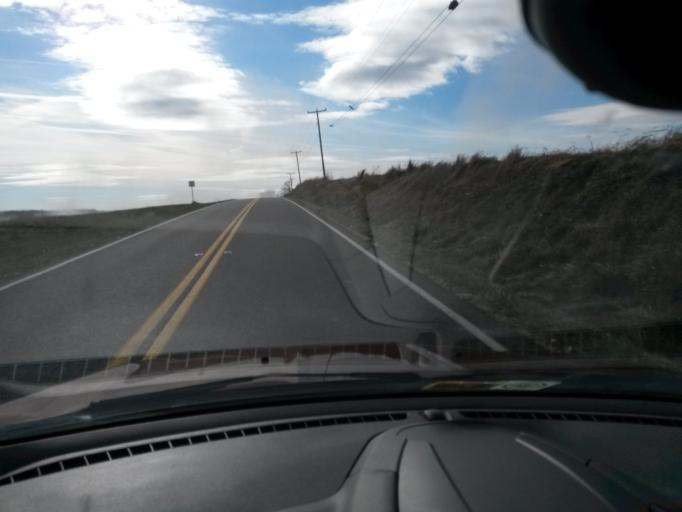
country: US
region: Virginia
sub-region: Rockingham County
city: Bridgewater
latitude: 38.3639
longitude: -79.0154
